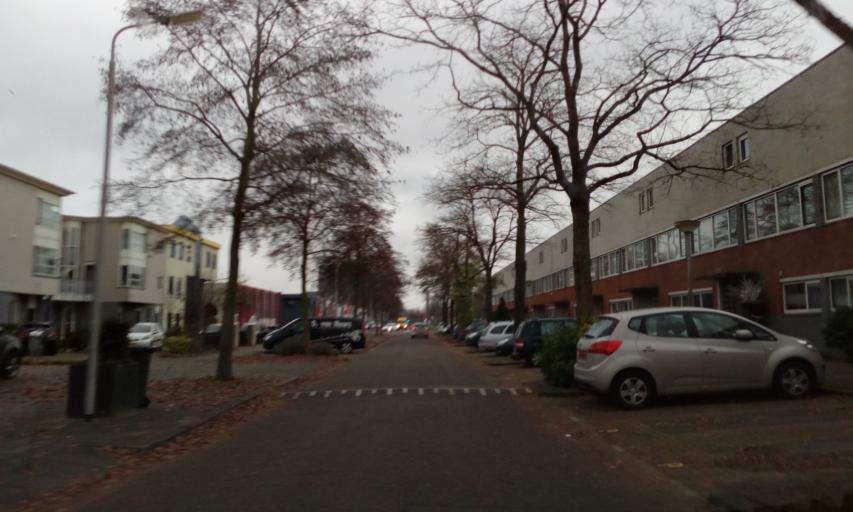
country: NL
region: South Holland
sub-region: Gemeente Delft
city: Delft
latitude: 51.9840
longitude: 4.3397
